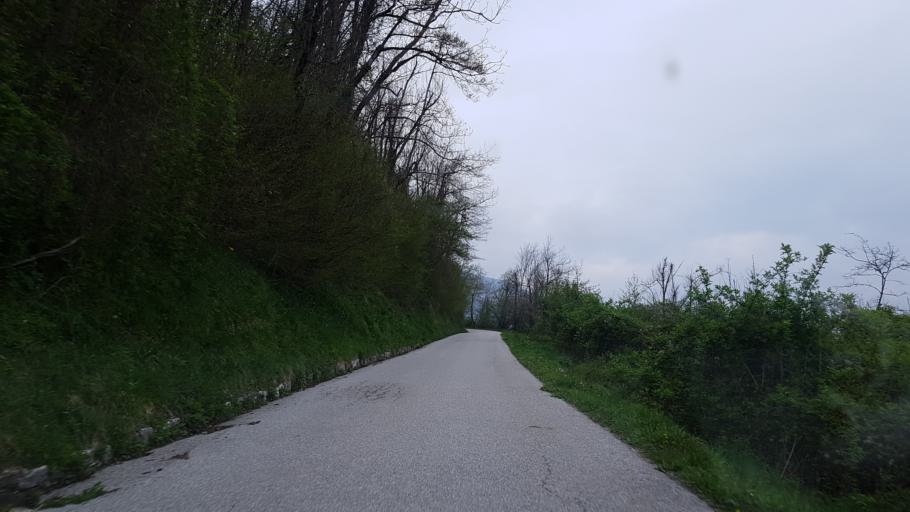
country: IT
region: Friuli Venezia Giulia
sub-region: Provincia di Udine
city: Taipana
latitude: 46.2514
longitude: 13.4303
